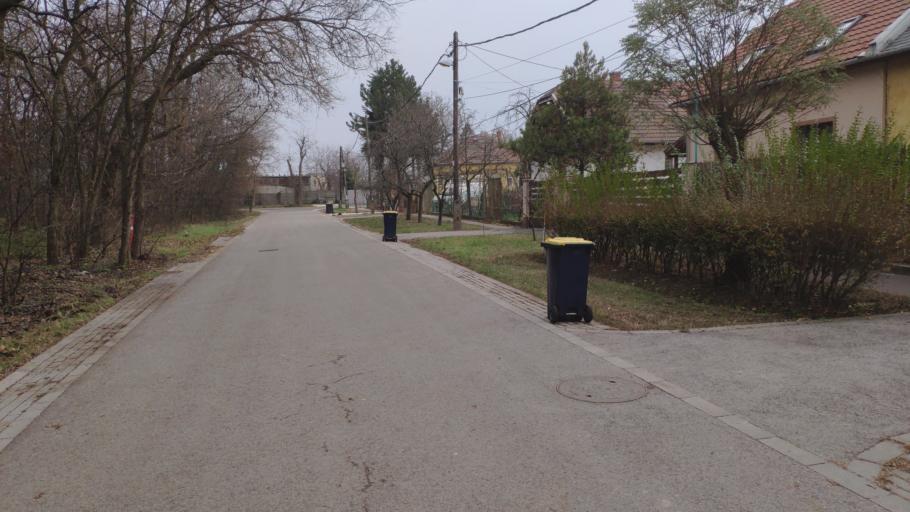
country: HU
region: Budapest
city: Budapest XVI. keruelet
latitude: 47.5114
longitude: 19.1578
